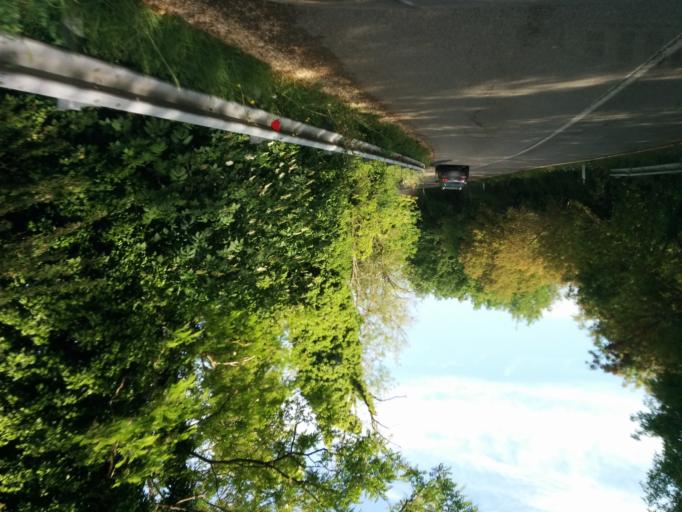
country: IT
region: Tuscany
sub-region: Province of Florence
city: San Casciano in Val di Pesa
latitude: 43.6431
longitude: 11.1776
